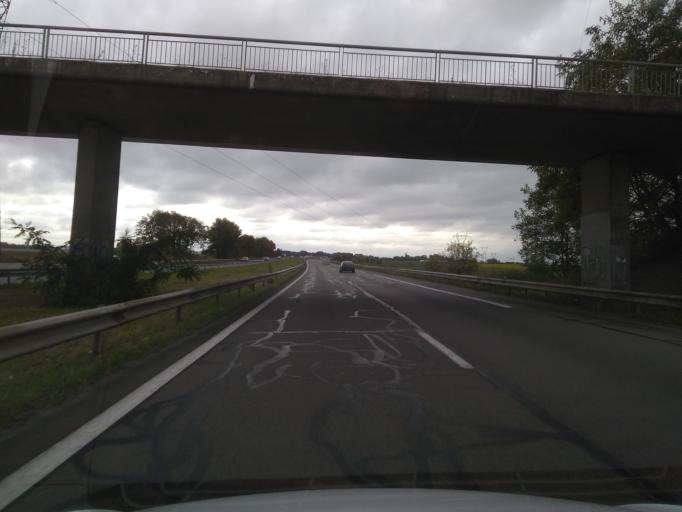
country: FR
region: Nord-Pas-de-Calais
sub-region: Departement du Nord
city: Orchies
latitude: 50.4890
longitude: 3.2137
